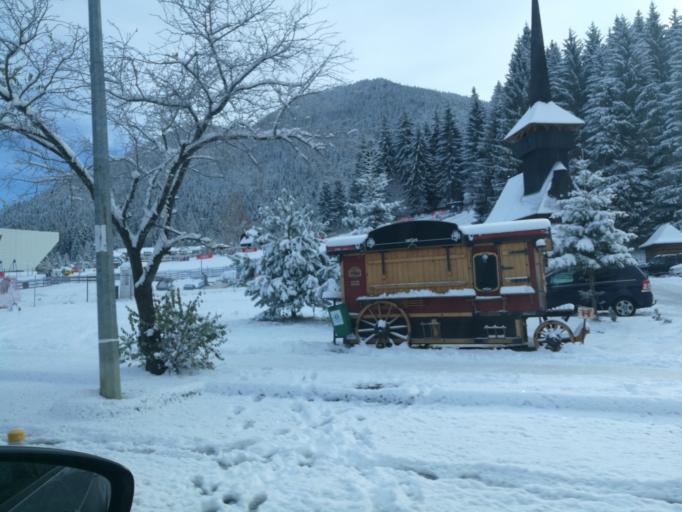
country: RO
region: Brasov
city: Brasov
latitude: 45.5929
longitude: 25.5522
